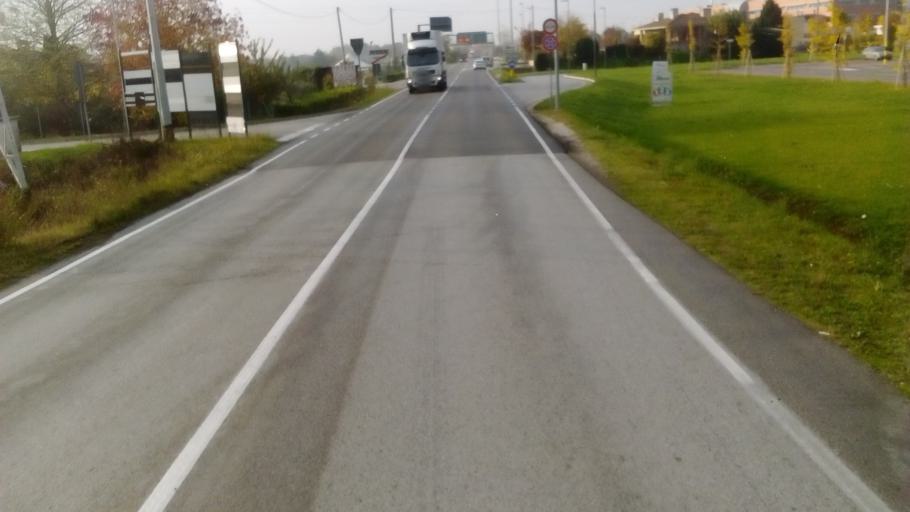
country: IT
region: Veneto
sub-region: Provincia di Vicenza
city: Dueville
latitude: 45.6353
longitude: 11.5712
